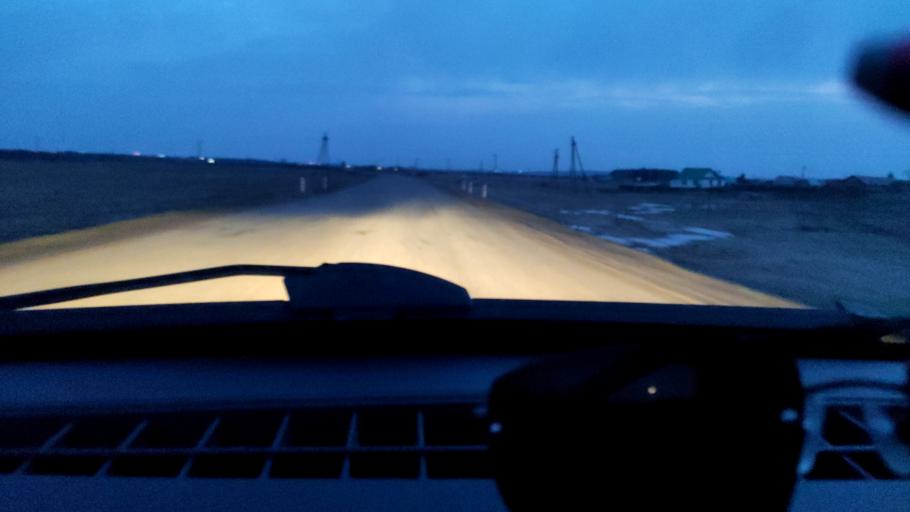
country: RU
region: Bashkortostan
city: Kabakovo
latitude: 54.4966
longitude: 56.1785
